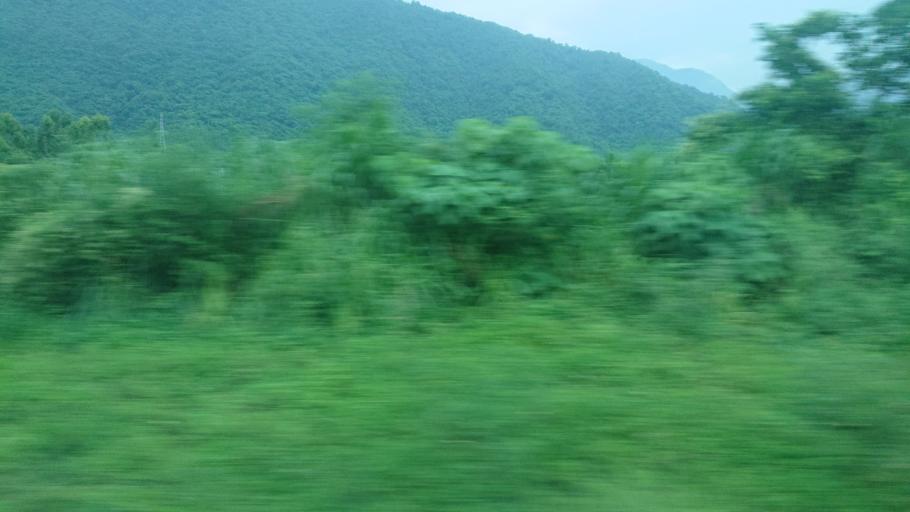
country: TW
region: Taiwan
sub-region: Hualien
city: Hualian
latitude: 24.1203
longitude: 121.6344
